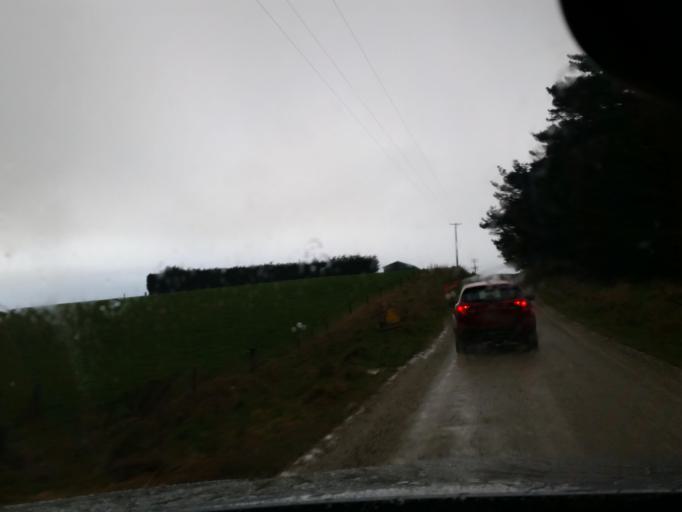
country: NZ
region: Southland
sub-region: Invercargill City
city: Invercargill
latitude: -46.3112
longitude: 168.4534
